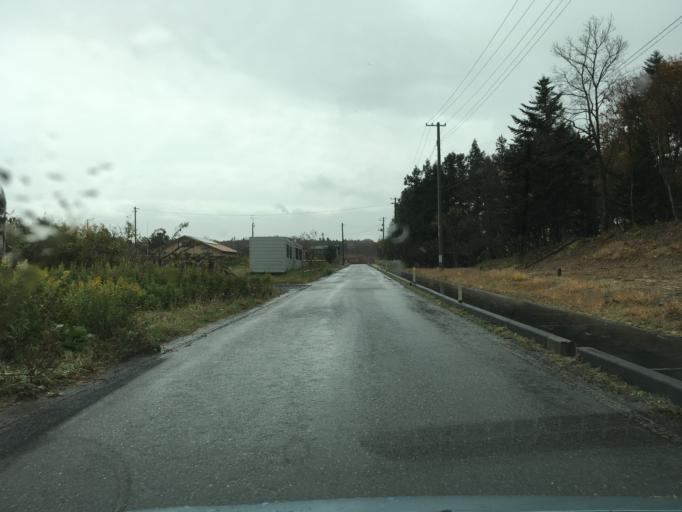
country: JP
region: Iwate
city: Ichinoseki
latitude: 38.7856
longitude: 141.2326
